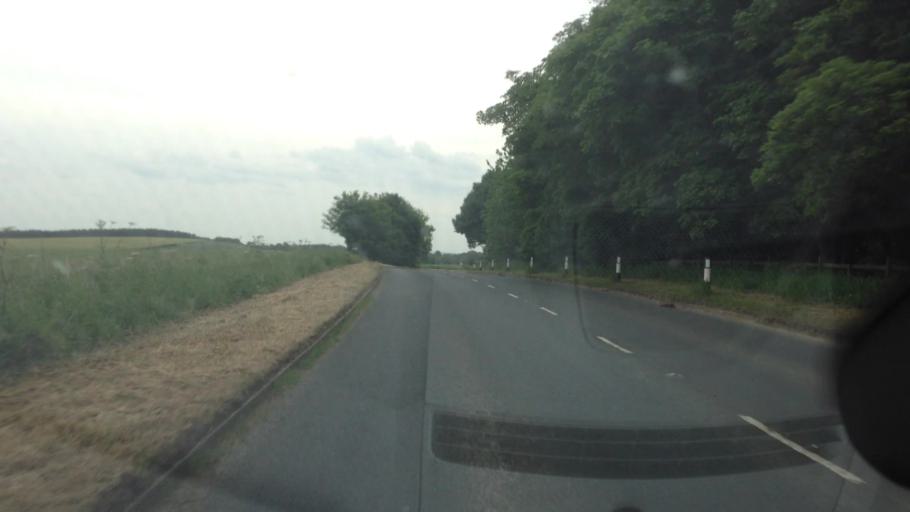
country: GB
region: England
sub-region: City and Borough of Wakefield
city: Woolley
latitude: 53.6111
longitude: -1.5333
